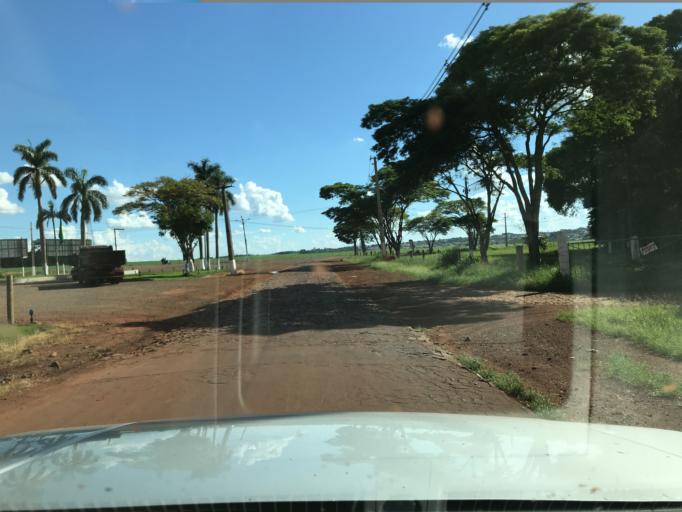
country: BR
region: Parana
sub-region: Palotina
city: Palotina
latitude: -24.2745
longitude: -53.8091
